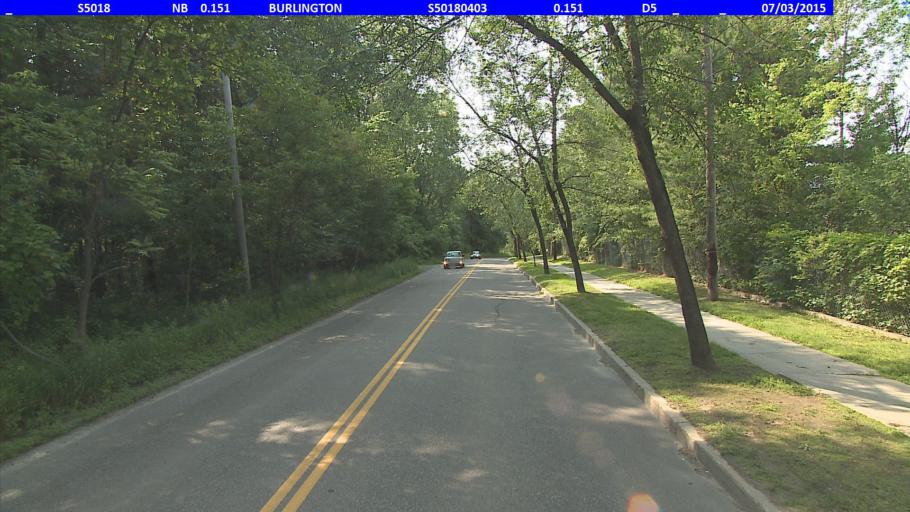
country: US
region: Vermont
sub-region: Chittenden County
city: Winooski
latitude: 44.4823
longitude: -73.1826
